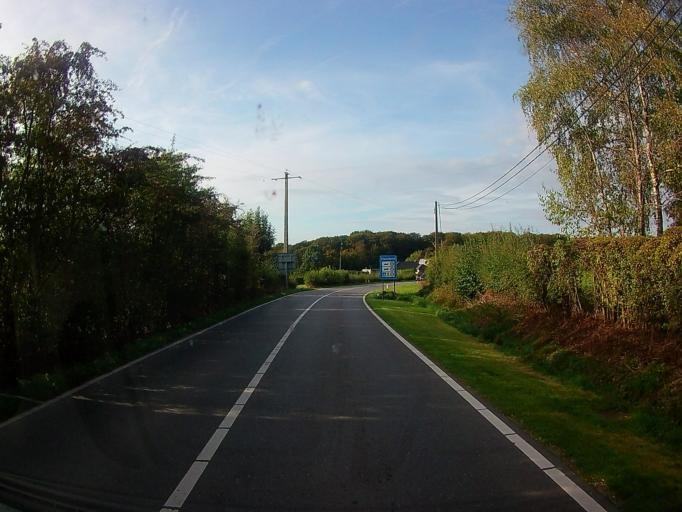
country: BE
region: Wallonia
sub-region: Province de Liege
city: Aubel
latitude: 50.7183
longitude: 5.8649
